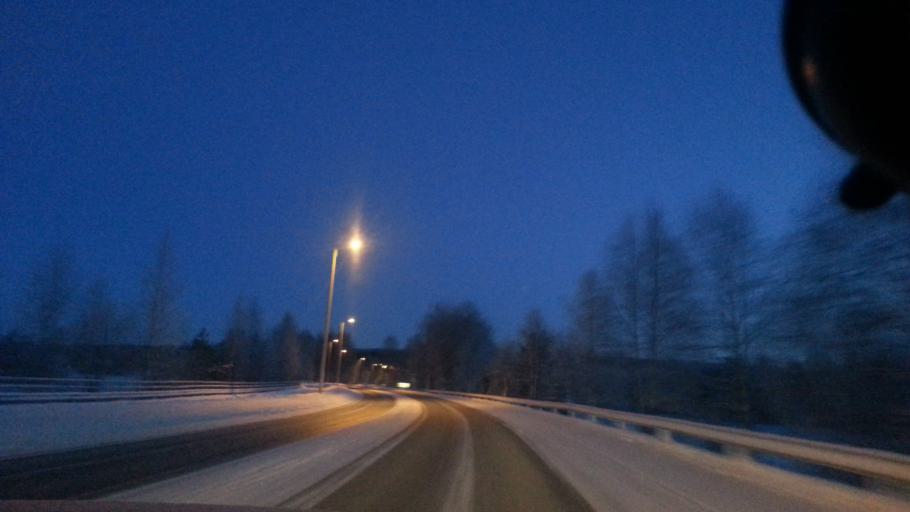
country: FI
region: Lapland
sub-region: Rovaniemi
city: Rovaniemi
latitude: 66.4844
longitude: 25.7491
